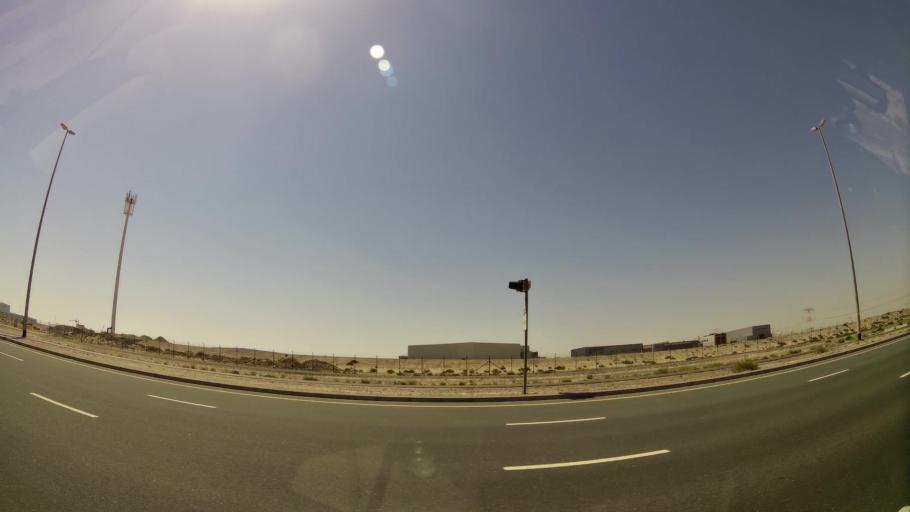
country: AE
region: Dubai
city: Dubai
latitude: 24.9322
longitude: 55.0962
